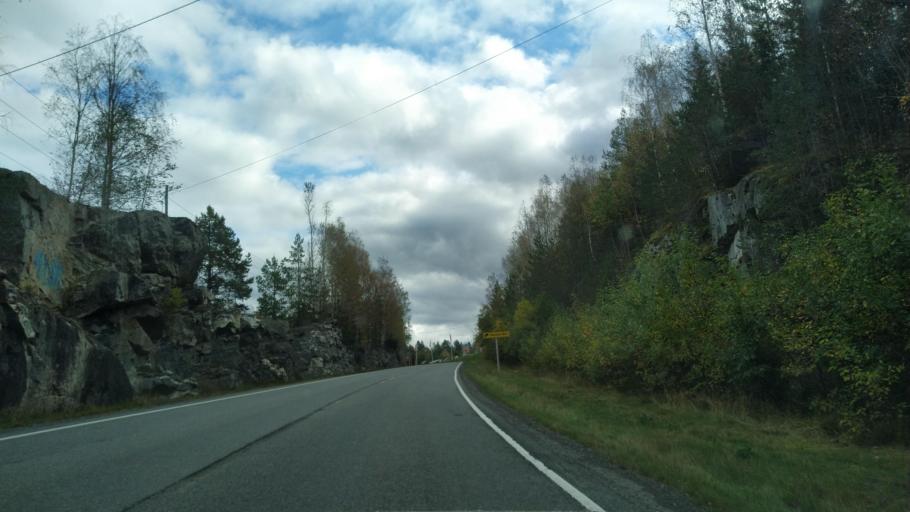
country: NO
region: Akershus
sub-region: Nes
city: Auli
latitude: 60.0345
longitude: 11.3470
